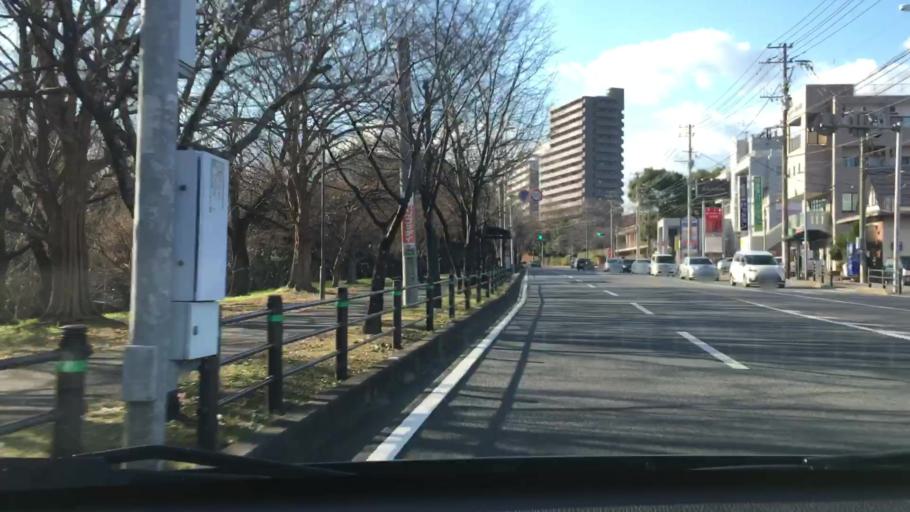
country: JP
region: Oita
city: Tsurusaki
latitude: 33.2254
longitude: 131.6576
